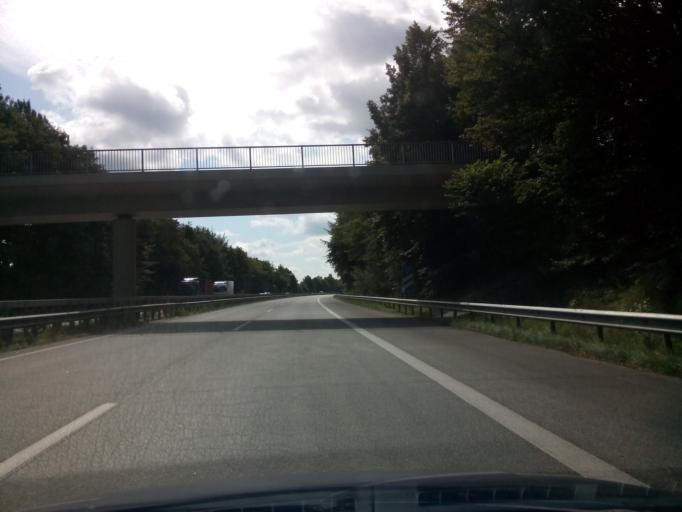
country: DE
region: Lower Saxony
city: Ritterhude
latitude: 53.1938
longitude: 8.6970
